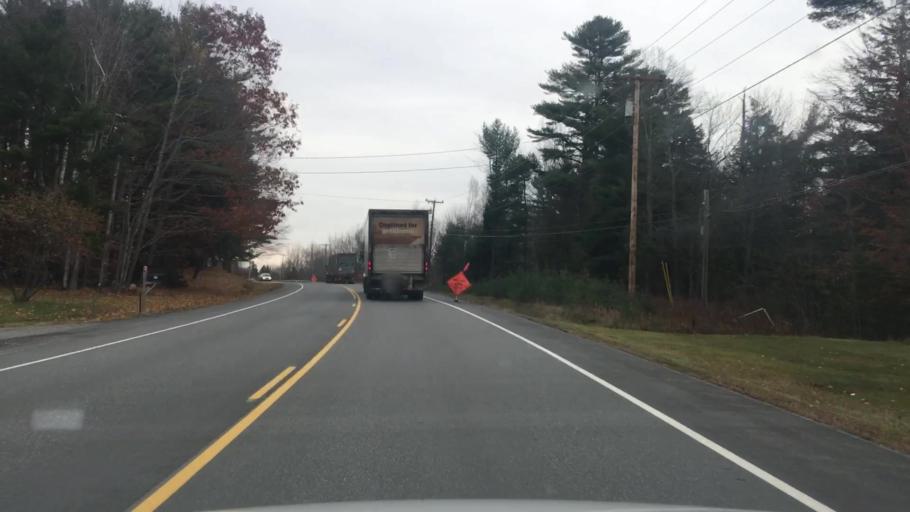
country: US
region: Maine
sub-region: Waldo County
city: Belfast
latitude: 44.4147
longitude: -69.0495
